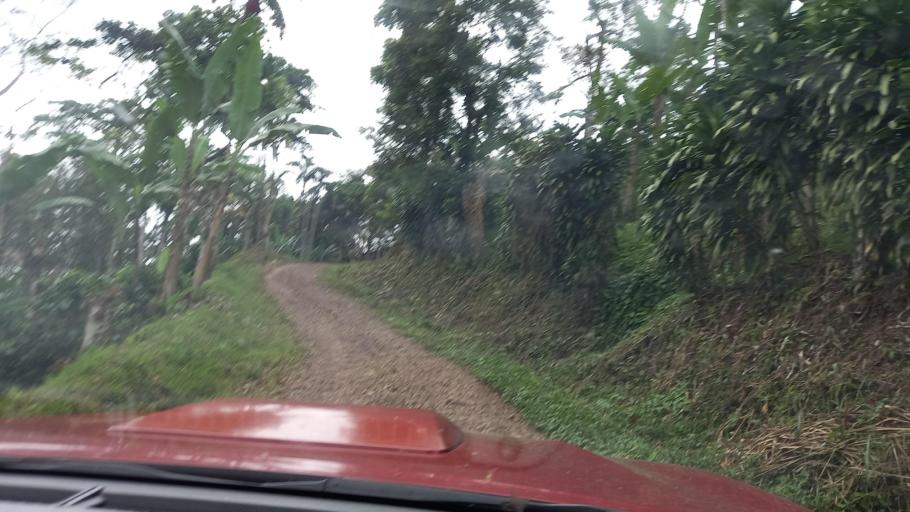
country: NI
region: Jinotega
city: San Jose de Bocay
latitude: 13.3388
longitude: -85.6580
